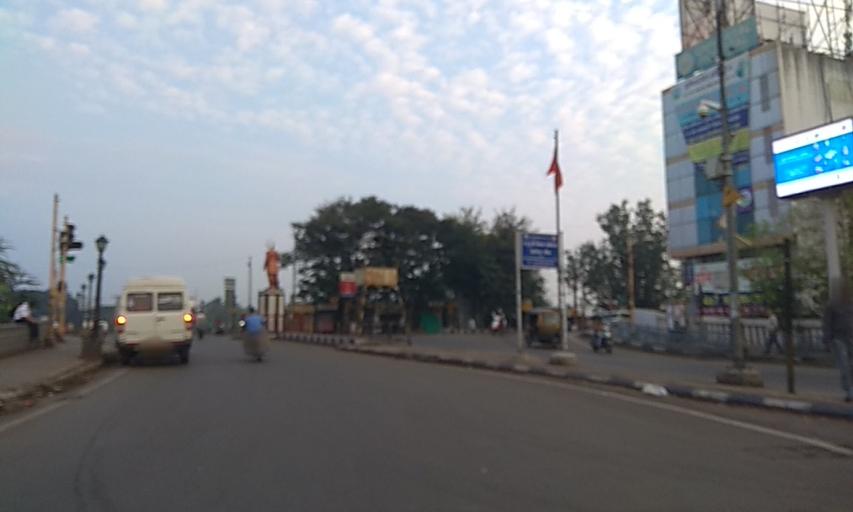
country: IN
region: Maharashtra
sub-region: Pune Division
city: Pune
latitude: 18.5211
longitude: 73.8552
